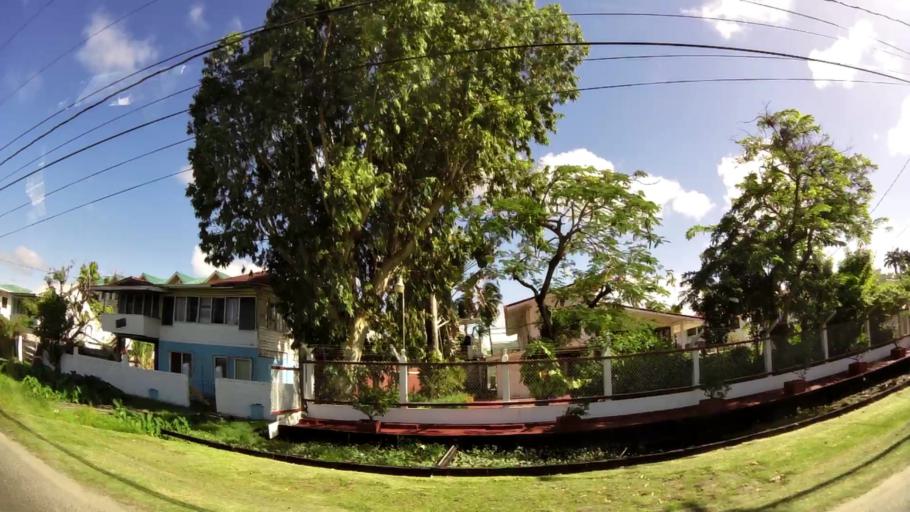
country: GY
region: Demerara-Mahaica
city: Georgetown
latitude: 6.8220
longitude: -58.1276
